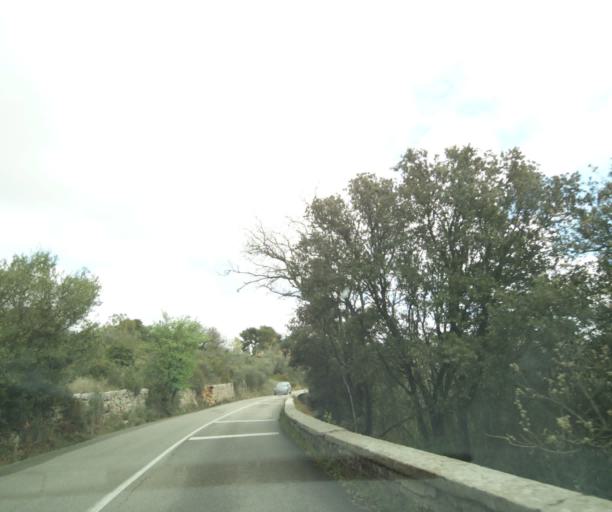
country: FR
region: Languedoc-Roussillon
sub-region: Departement de l'Herault
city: Pignan
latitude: 43.5870
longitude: 3.7542
